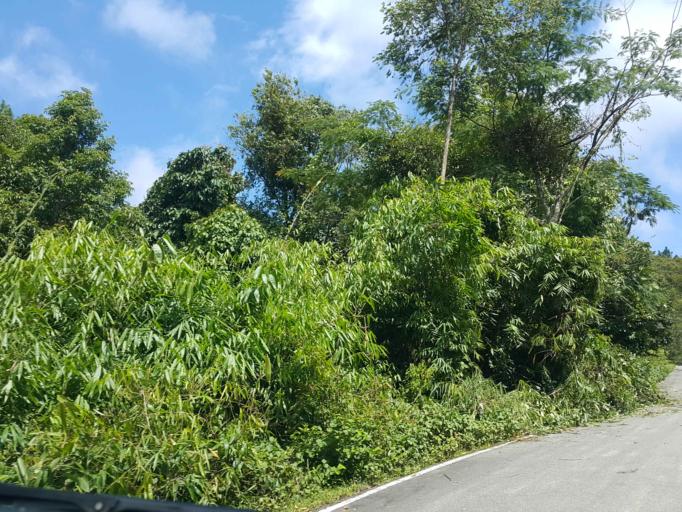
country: TH
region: Chiang Mai
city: Mae Chaem
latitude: 18.5150
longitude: 98.5253
